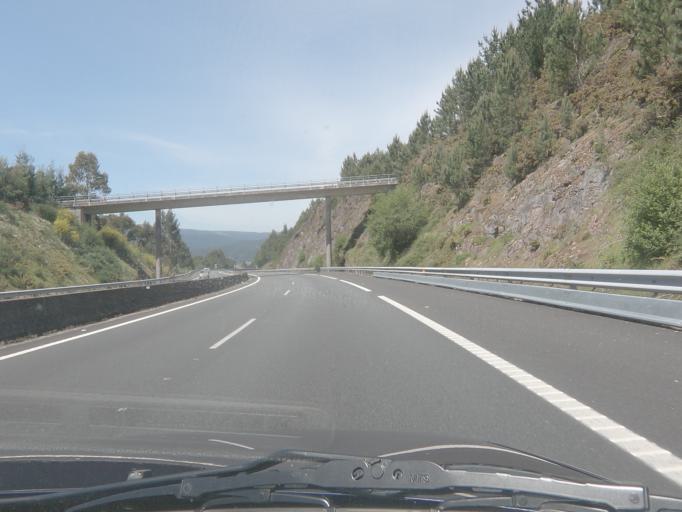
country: ES
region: Galicia
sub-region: Provincia de Pontevedra
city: Valga
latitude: 42.7042
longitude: -8.6389
